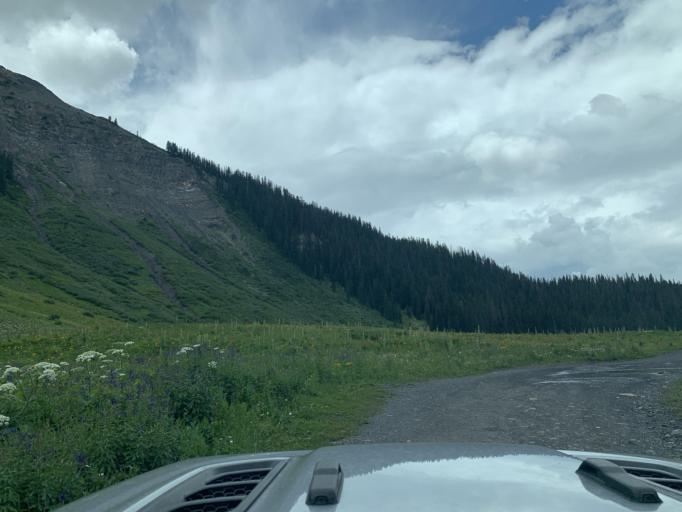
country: US
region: Colorado
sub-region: Gunnison County
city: Crested Butte
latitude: 39.0078
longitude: -107.0397
